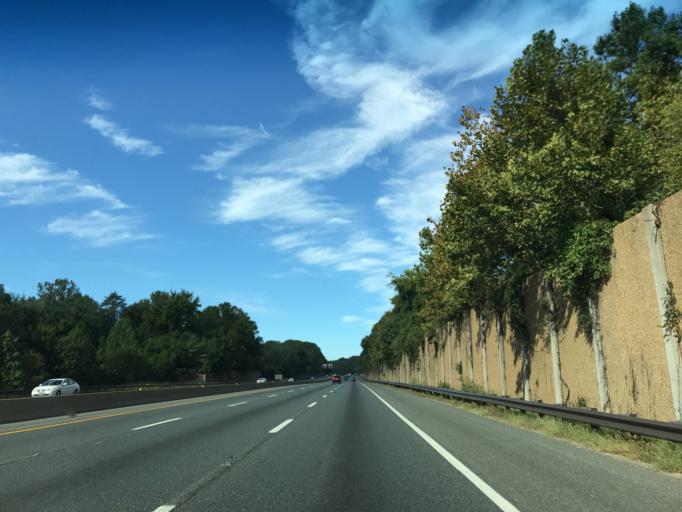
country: US
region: Maryland
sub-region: Anne Arundel County
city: Riva
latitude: 38.9843
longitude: -76.5885
